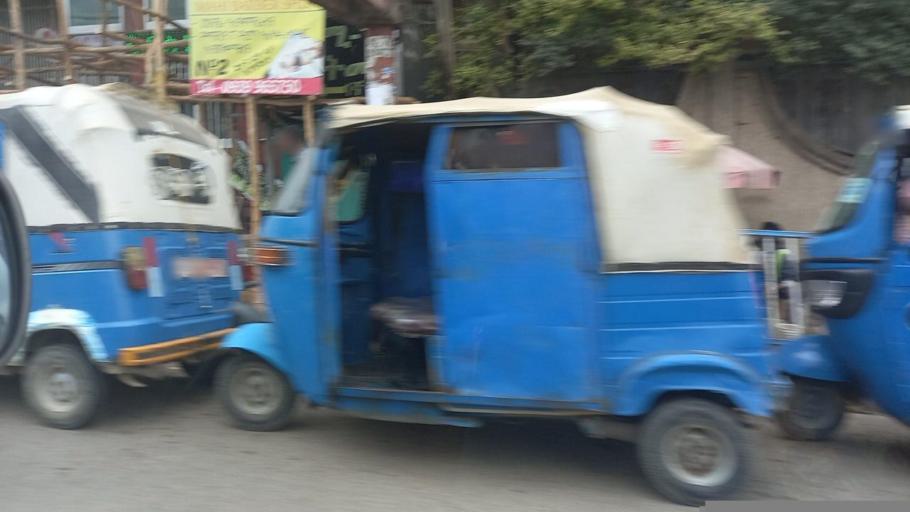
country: ET
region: Adis Abeba
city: Addis Ababa
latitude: 9.0110
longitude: 38.8366
